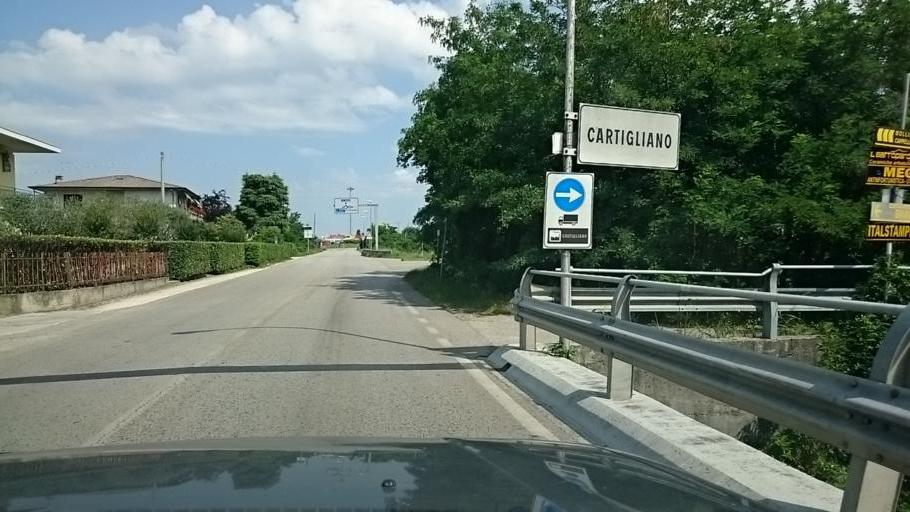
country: IT
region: Veneto
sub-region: Provincia di Vicenza
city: Cartigliano
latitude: 45.7227
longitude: 11.6947
